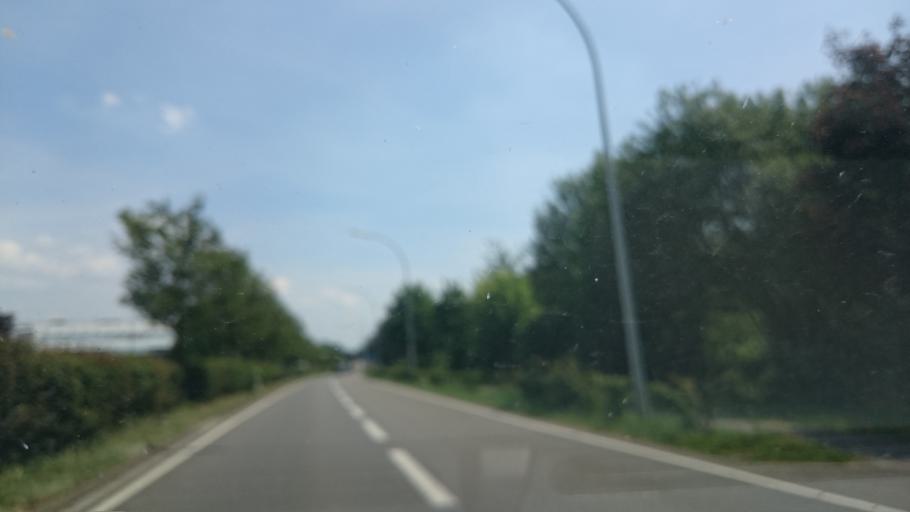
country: LU
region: Luxembourg
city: Capellen
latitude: 49.6406
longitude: 6.0040
